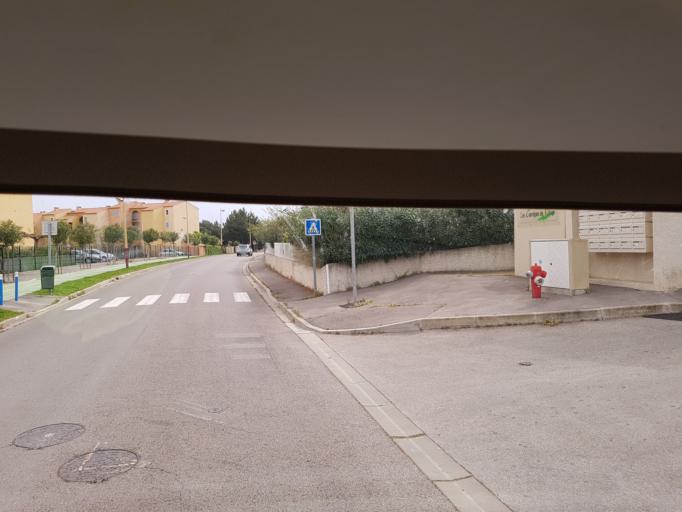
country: FR
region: Languedoc-Roussillon
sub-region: Departement de l'Aude
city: Fleury
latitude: 43.1873
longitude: 3.1905
